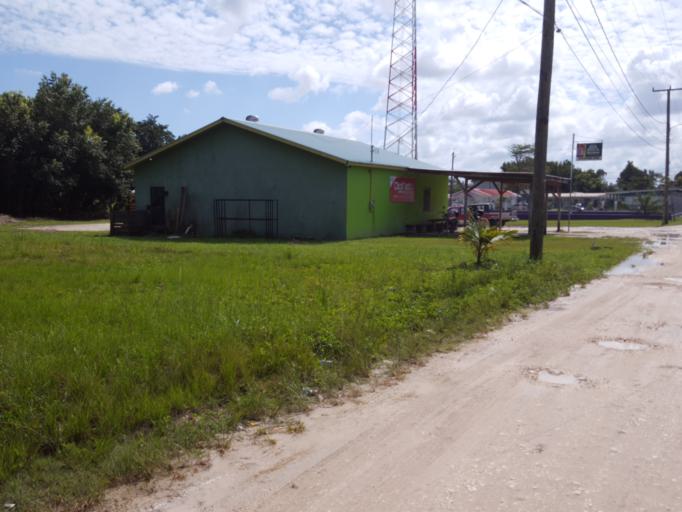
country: BZ
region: Belize
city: Belize City
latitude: 17.5703
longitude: -88.4036
